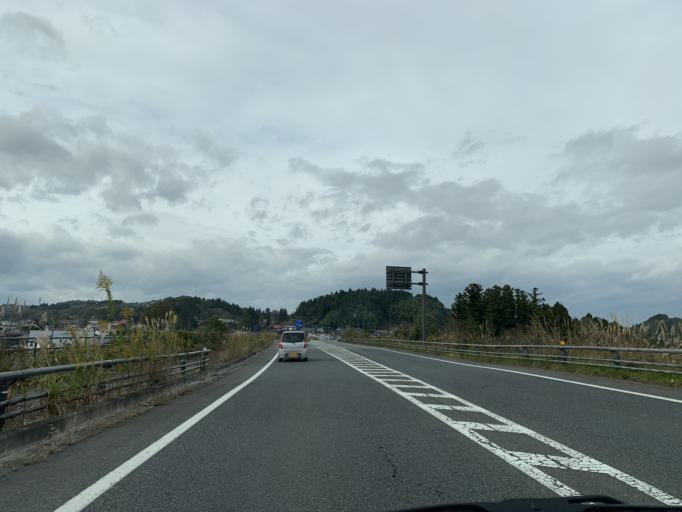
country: JP
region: Iwate
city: Ichinoseki
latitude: 39.0132
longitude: 141.1166
